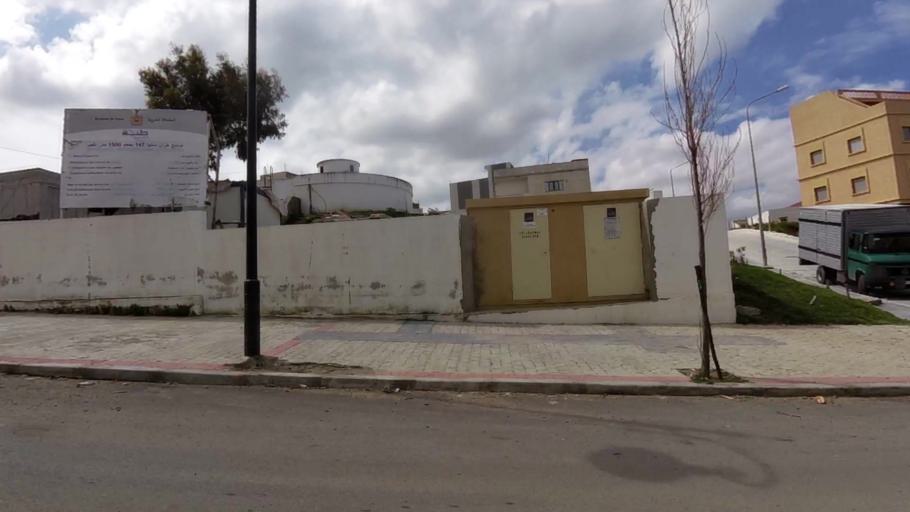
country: MA
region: Tanger-Tetouan
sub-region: Tanger-Assilah
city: Tangier
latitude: 35.7757
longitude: -5.7509
